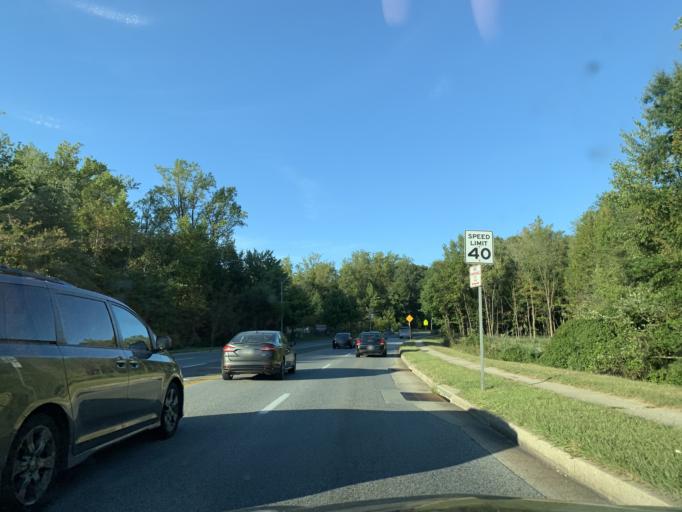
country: US
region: Maryland
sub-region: Baltimore County
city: Perry Hall
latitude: 39.3858
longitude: -76.4597
